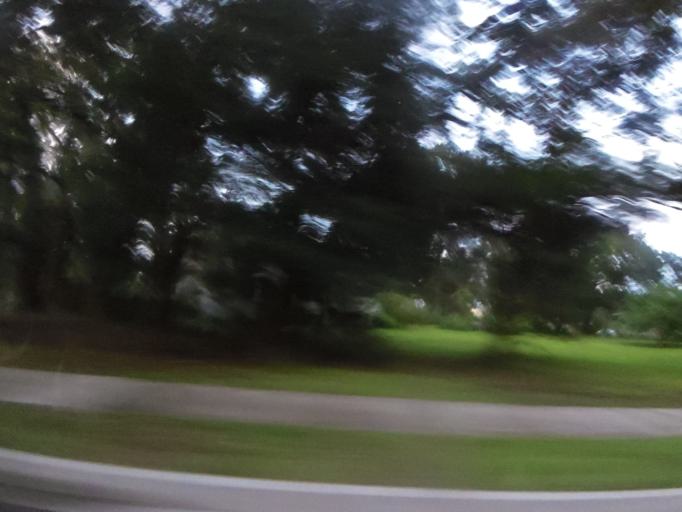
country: US
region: Florida
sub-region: Duval County
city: Jacksonville
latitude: 30.3649
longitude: -81.5565
